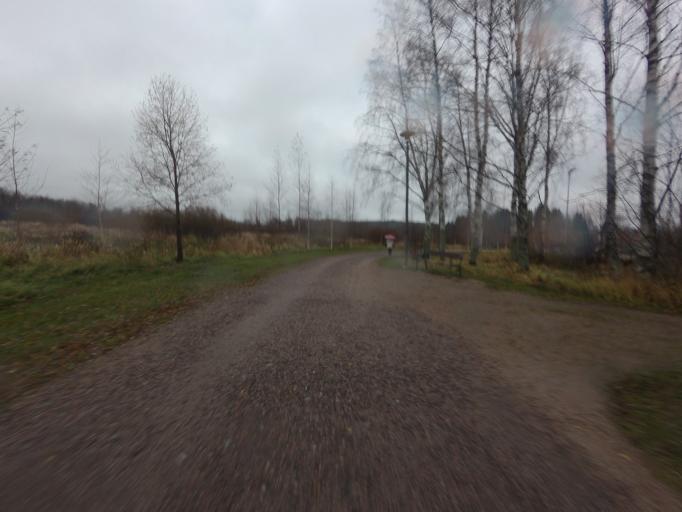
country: FI
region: Uusimaa
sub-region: Helsinki
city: Espoo
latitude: 60.2104
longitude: 24.6649
